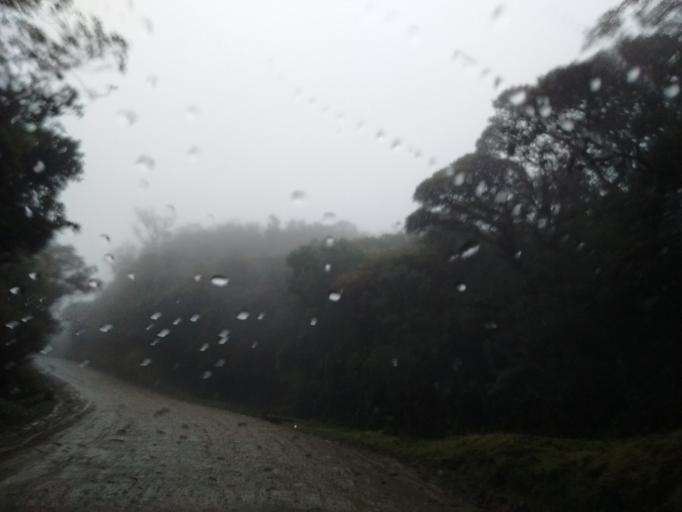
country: CO
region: Cauca
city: Paispamba
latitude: 2.1614
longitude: -76.4200
